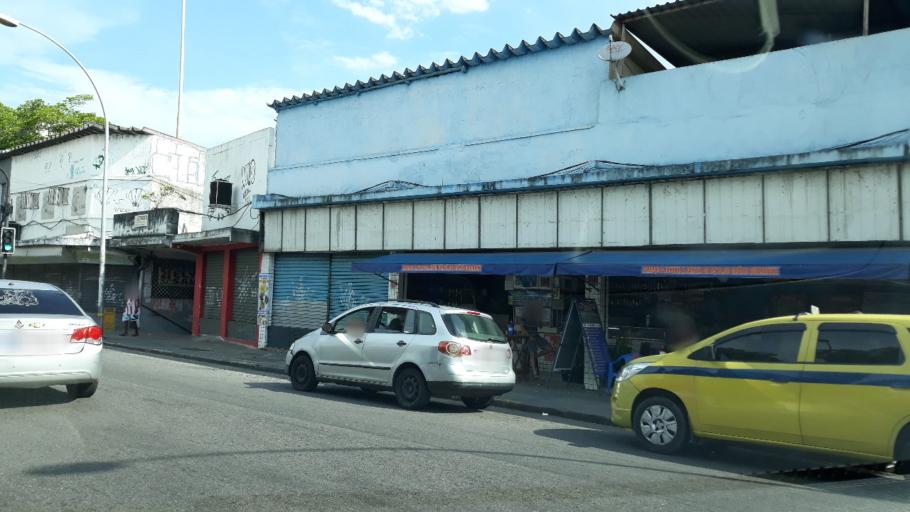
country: BR
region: Rio de Janeiro
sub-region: Duque De Caxias
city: Duque de Caxias
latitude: -22.8400
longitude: -43.2782
